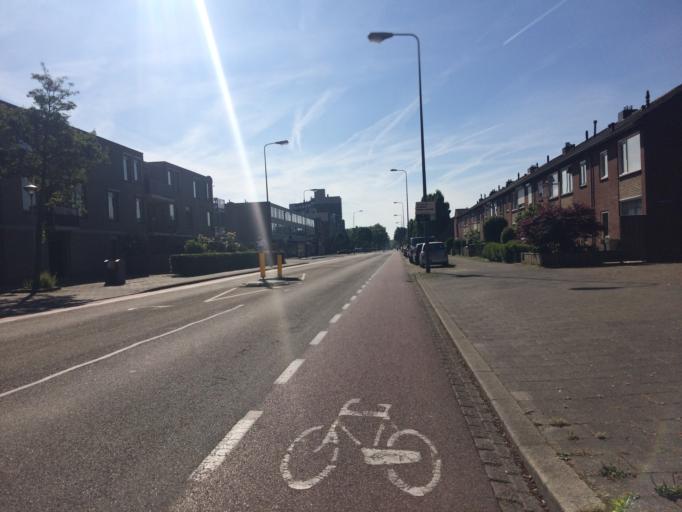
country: NL
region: North Brabant
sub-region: Gemeente 's-Hertogenbosch
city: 's-Hertogenbosch
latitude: 51.7017
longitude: 5.2586
